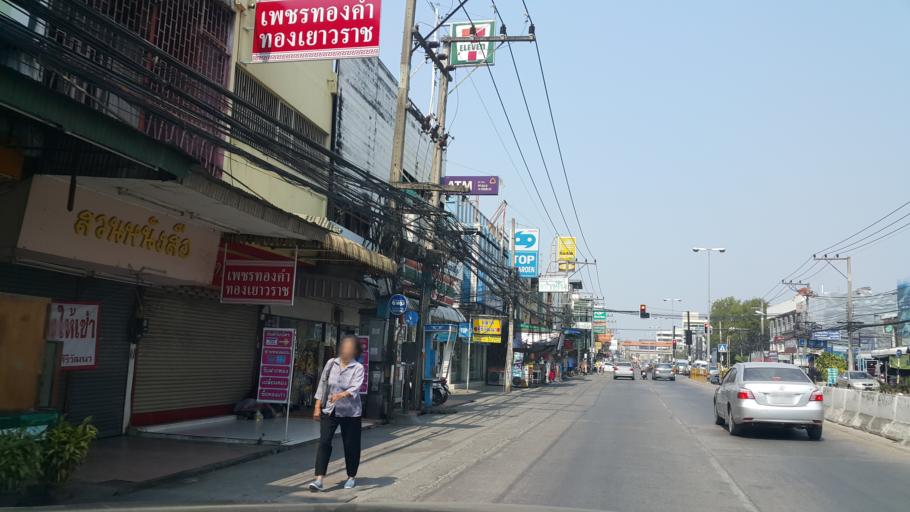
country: TH
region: Chiang Mai
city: Chiang Mai
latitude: 18.8045
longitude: 98.9854
